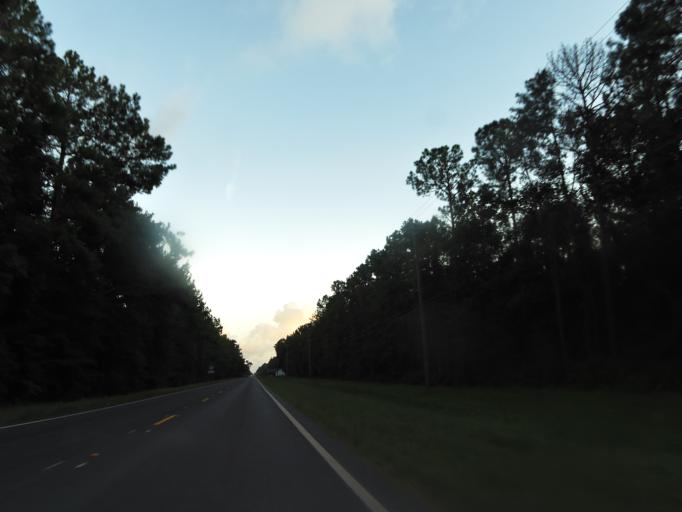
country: US
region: Georgia
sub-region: Camden County
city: Kingsland
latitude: 30.8707
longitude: -81.7046
